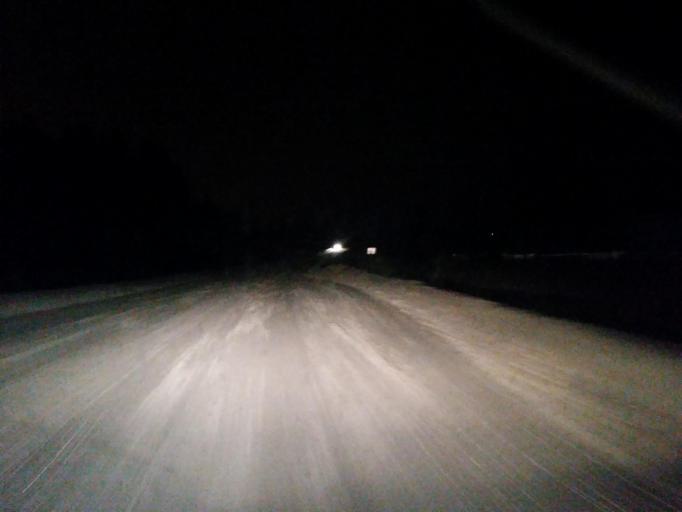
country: SE
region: Norrbotten
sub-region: Alvsbyns Kommun
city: AElvsbyn
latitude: 65.6711
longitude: 20.9536
